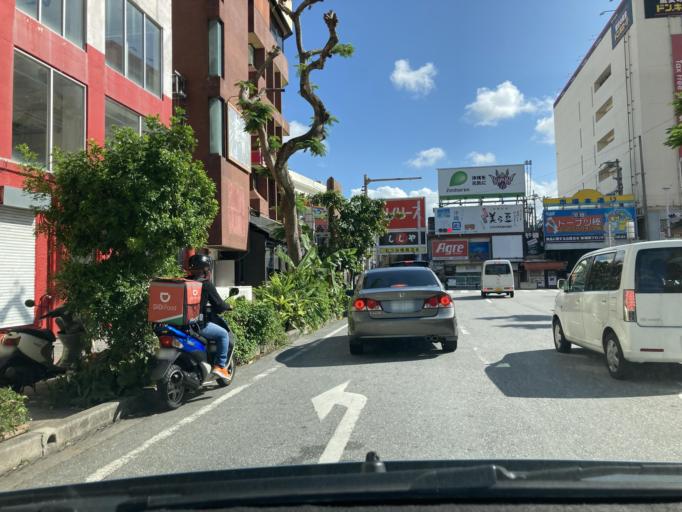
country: JP
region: Okinawa
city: Naha-shi
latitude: 26.2167
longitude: 127.6879
